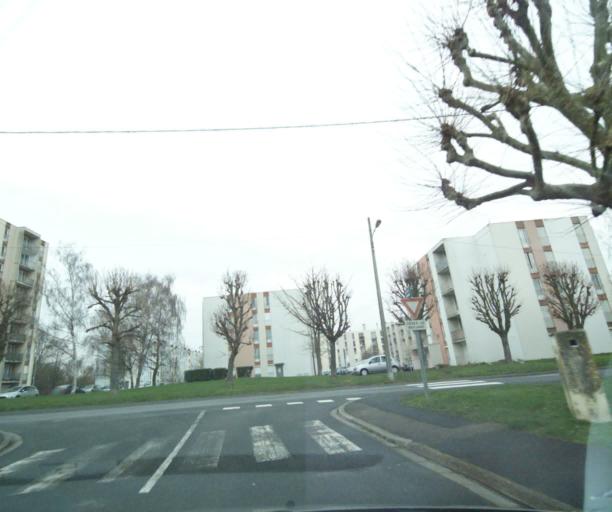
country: FR
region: Picardie
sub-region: Departement de l'Oise
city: Noyon
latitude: 49.5774
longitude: 2.9876
